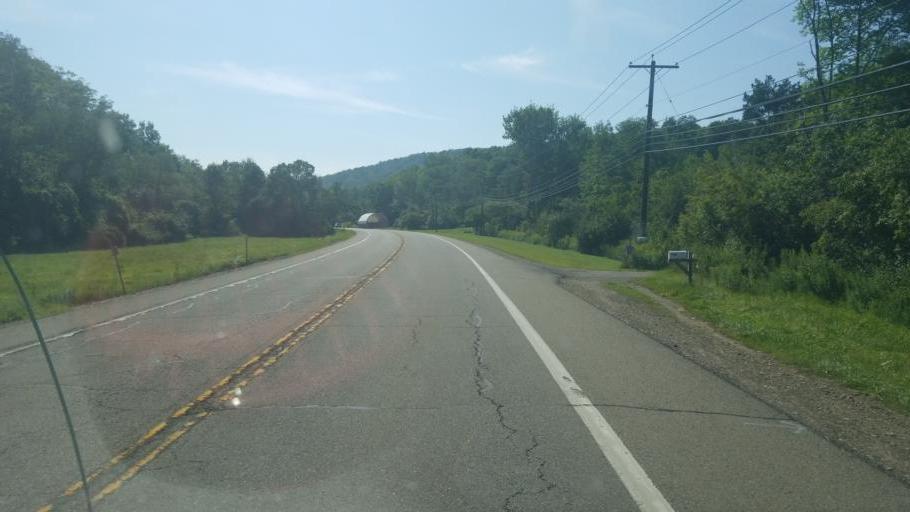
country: US
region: New York
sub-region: Allegany County
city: Wellsville
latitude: 42.1242
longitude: -77.9933
